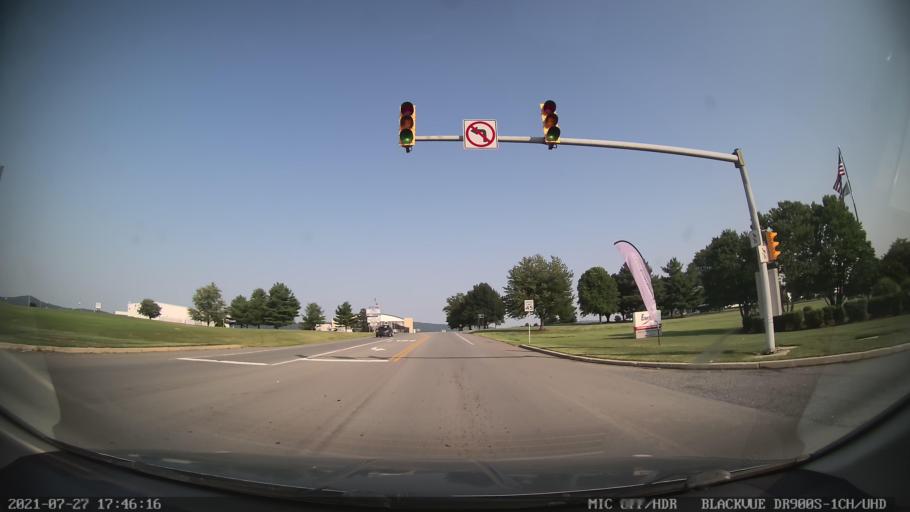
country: US
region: Pennsylvania
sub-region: Berks County
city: River View Park
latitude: 40.3724
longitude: -75.9661
